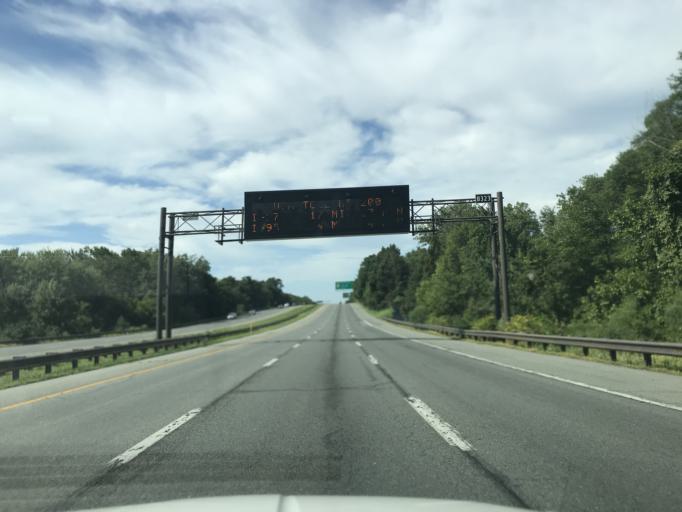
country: US
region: Maryland
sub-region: Montgomery County
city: Burtonsville
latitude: 39.0939
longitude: -76.9397
